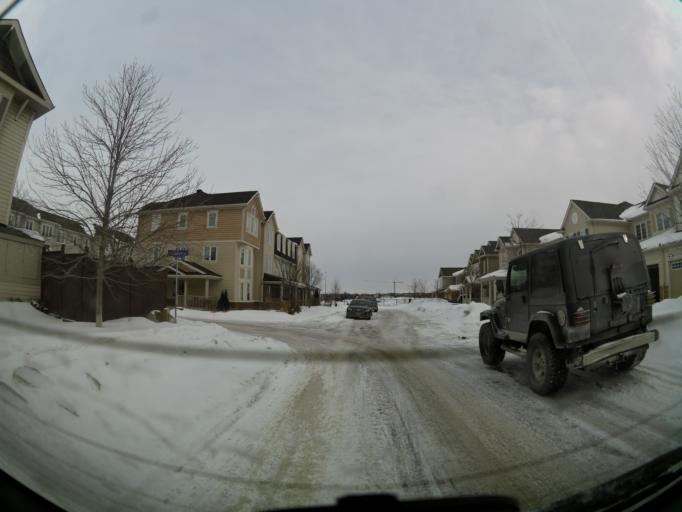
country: CA
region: Ontario
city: Bells Corners
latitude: 45.2897
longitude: -75.9178
